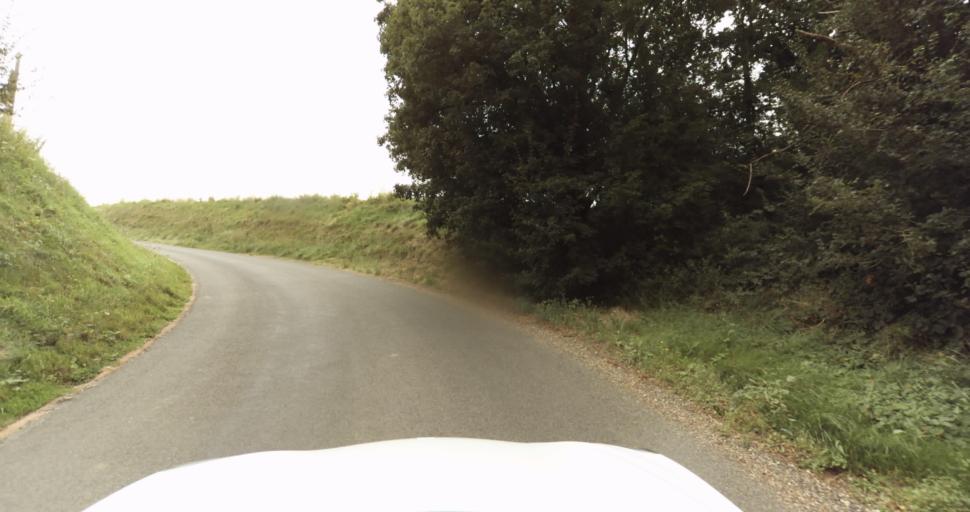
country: FR
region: Haute-Normandie
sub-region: Departement de l'Eure
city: Saint-Sebastien-de-Morsent
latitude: 49.0159
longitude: 1.0624
